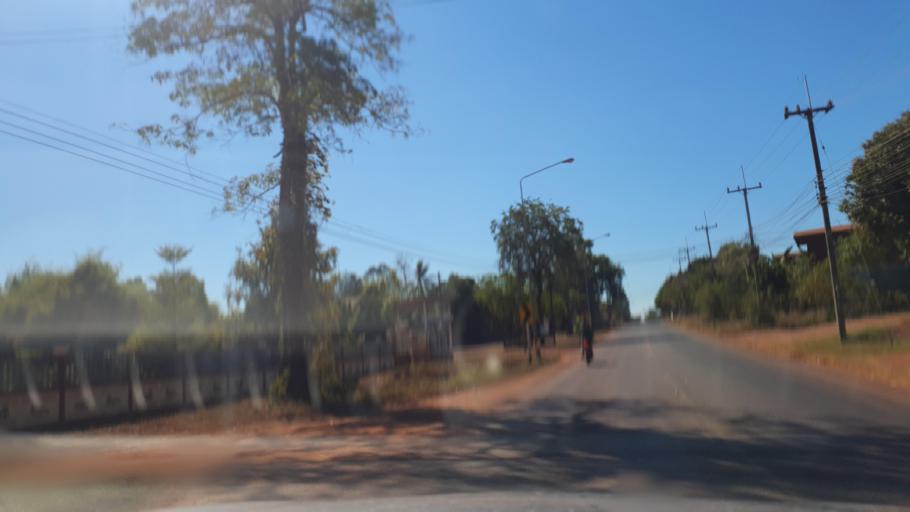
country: TH
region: Nakhon Phanom
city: Si Songkhram
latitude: 17.7593
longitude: 104.2865
